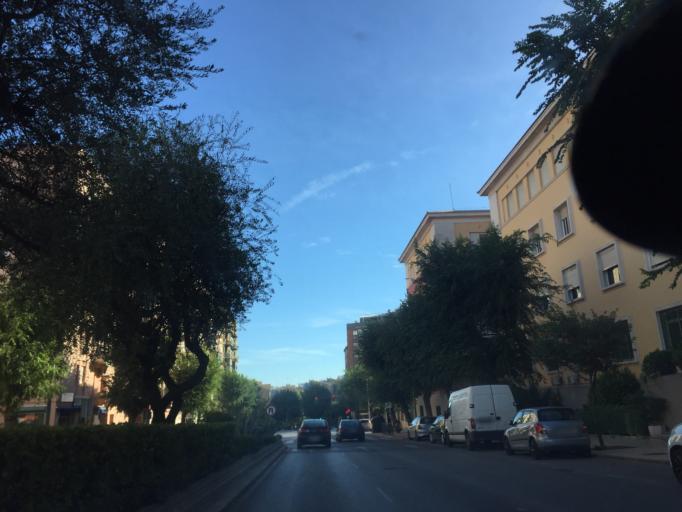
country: ES
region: Andalusia
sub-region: Provincia de Jaen
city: Jaen
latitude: 37.7779
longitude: -3.7868
